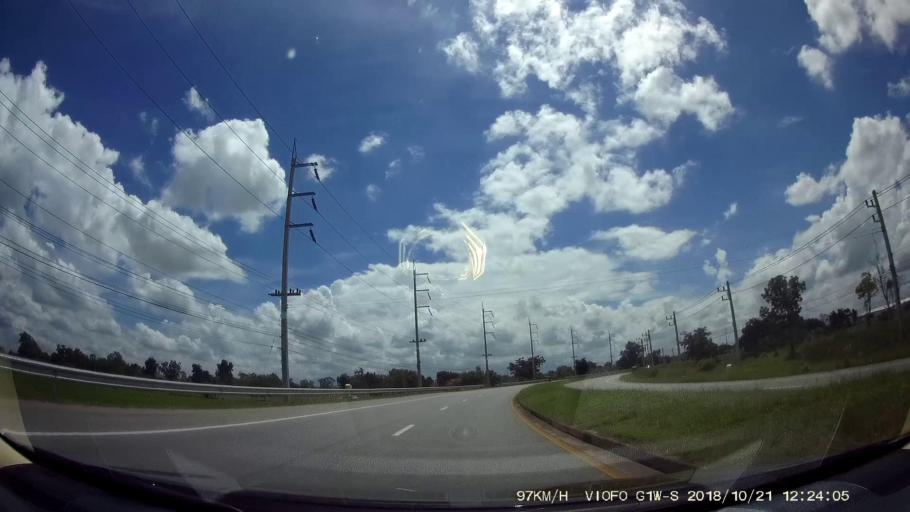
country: TH
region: Nakhon Ratchasima
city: Dan Khun Thot
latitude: 15.2372
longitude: 101.7866
